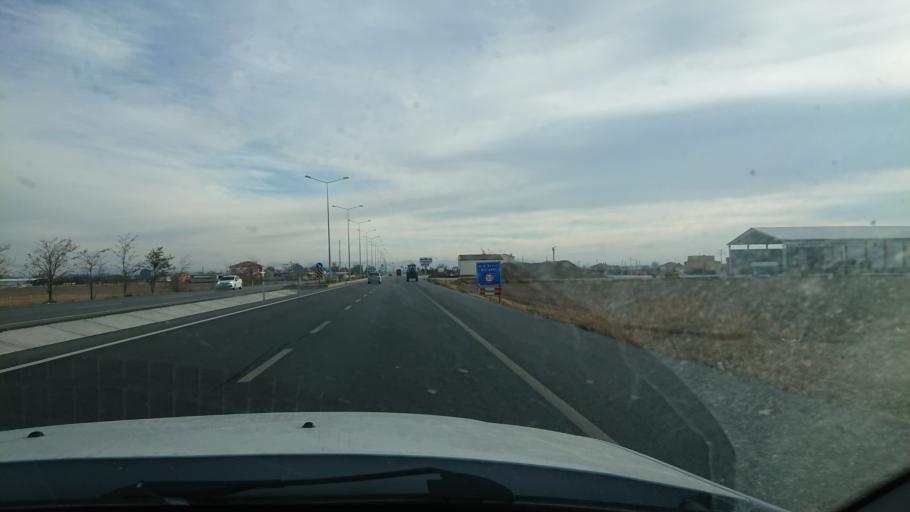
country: TR
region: Aksaray
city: Yesilova
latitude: 38.2893
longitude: 33.7528
